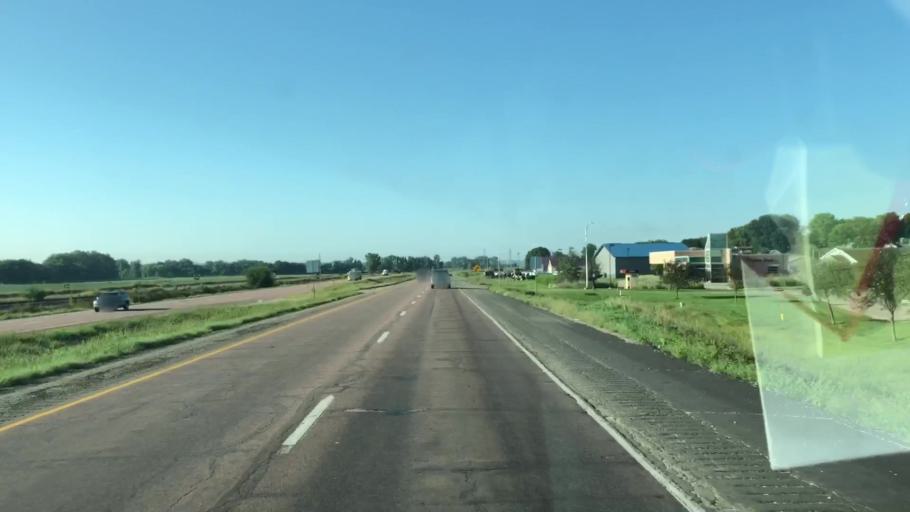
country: US
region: Iowa
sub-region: Woodbury County
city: Sioux City
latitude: 42.6176
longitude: -96.2948
